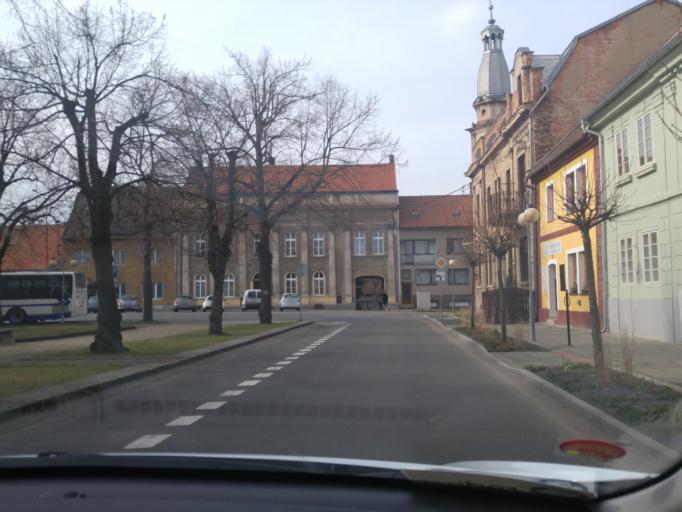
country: CZ
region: Central Bohemia
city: Kostelec nad Labem
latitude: 50.2313
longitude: 14.5891
